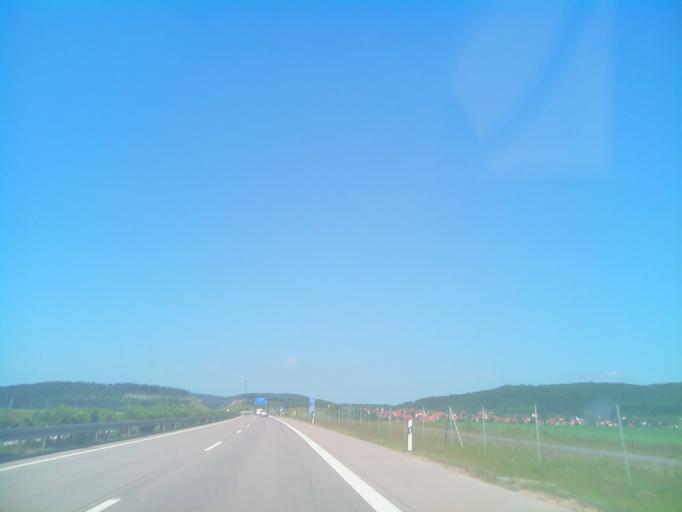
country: DE
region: Thuringia
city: Wolfershausen
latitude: 50.4412
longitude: 10.4393
